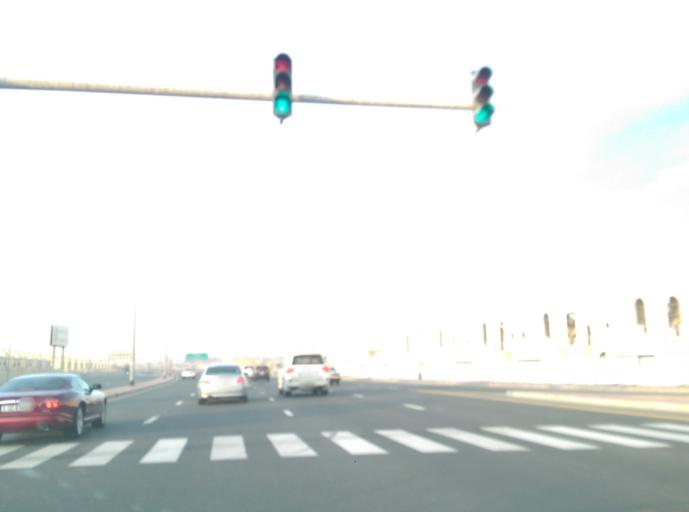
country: AE
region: Dubai
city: Dubai
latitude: 25.0523
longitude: 55.1707
